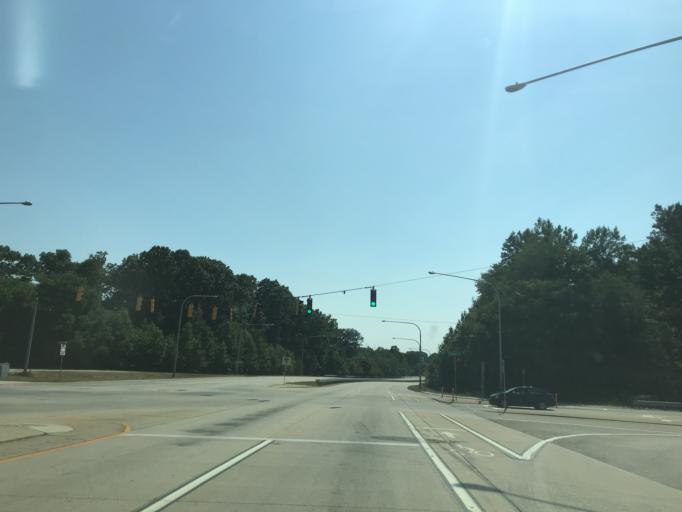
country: US
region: Delaware
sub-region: New Castle County
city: Brookside
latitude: 39.6856
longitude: -75.7066
